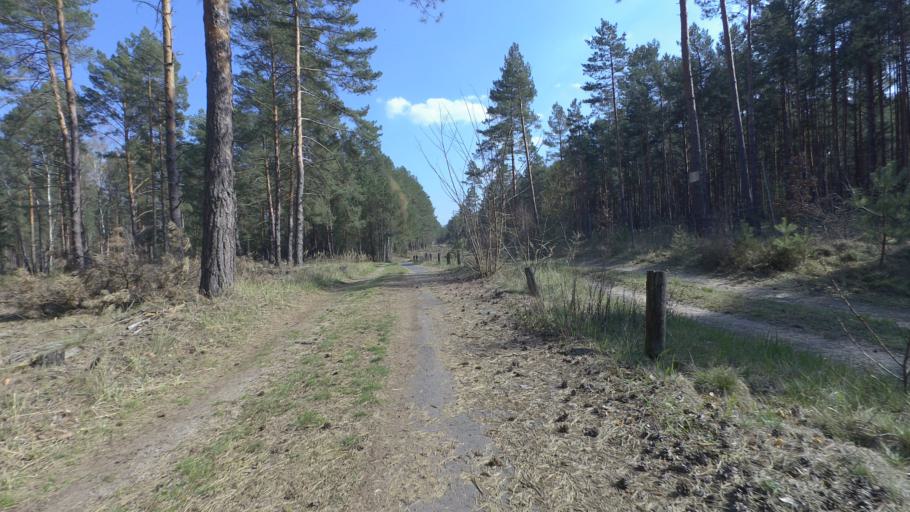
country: DE
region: Brandenburg
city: Mittenwalde
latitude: 52.1900
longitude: 13.5295
